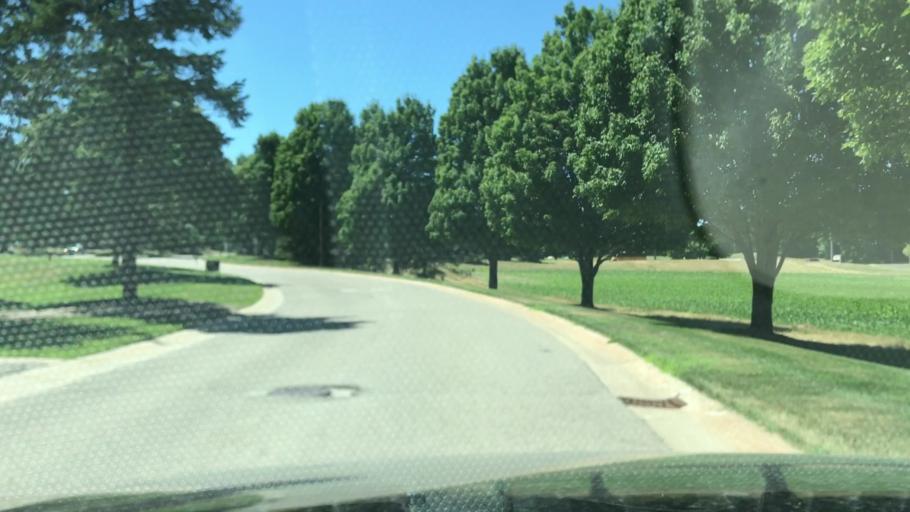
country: US
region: Michigan
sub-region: Ottawa County
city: Holland
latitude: 42.7723
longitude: -86.0750
